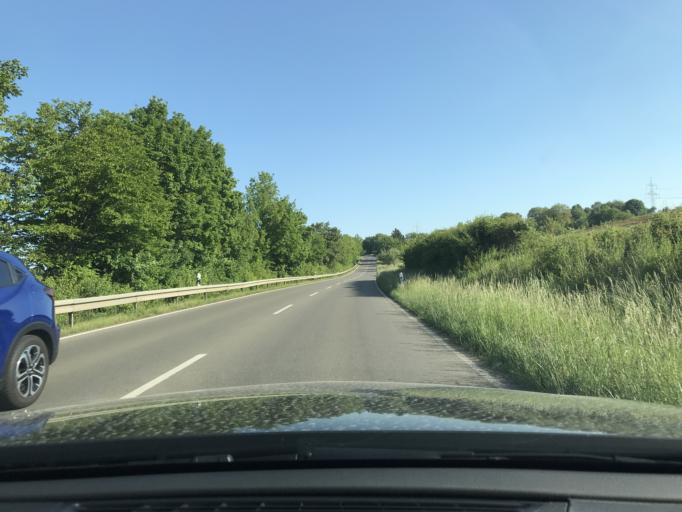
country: DE
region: Baden-Wuerttemberg
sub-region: Regierungsbezirk Stuttgart
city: Schwaikheim
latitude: 48.8811
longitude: 9.3175
